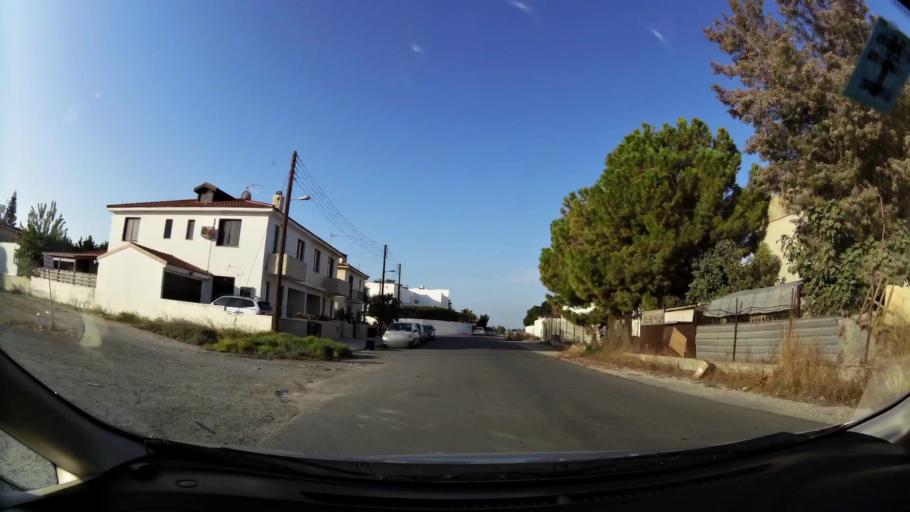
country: CY
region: Larnaka
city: Aradippou
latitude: 34.9339
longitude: 33.5920
